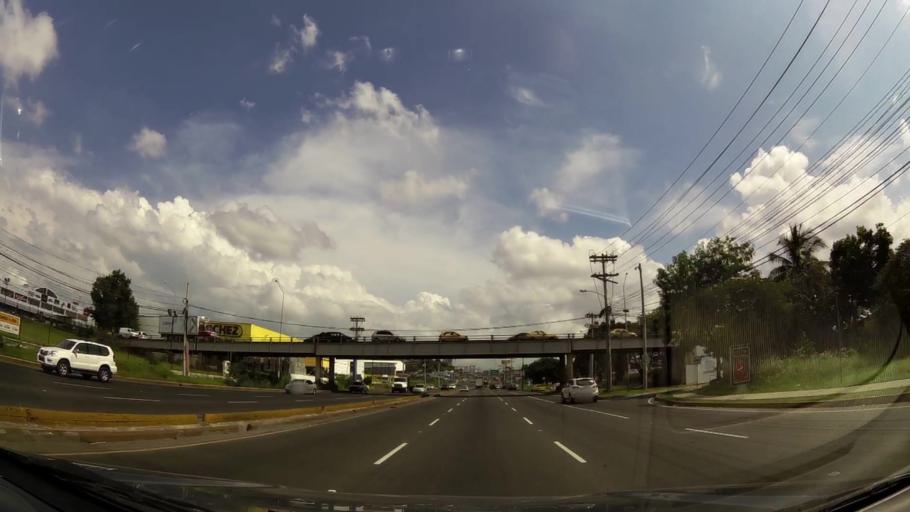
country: PA
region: Panama
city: San Miguelito
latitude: 9.0392
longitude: -79.4786
